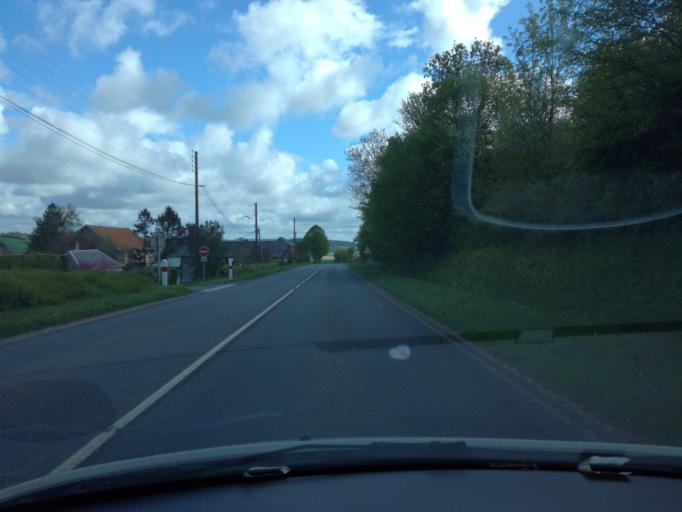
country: FR
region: Picardie
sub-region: Departement de la Somme
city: Hornoy-le-Bourg
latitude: 49.8576
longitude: 1.9572
